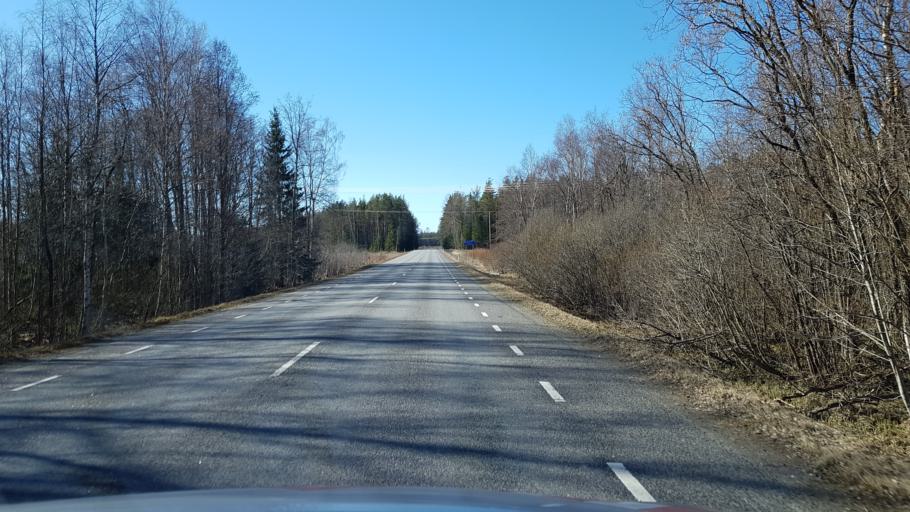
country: EE
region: Laeaene-Virumaa
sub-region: Viru-Nigula vald
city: Kunda
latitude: 59.3653
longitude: 26.6098
